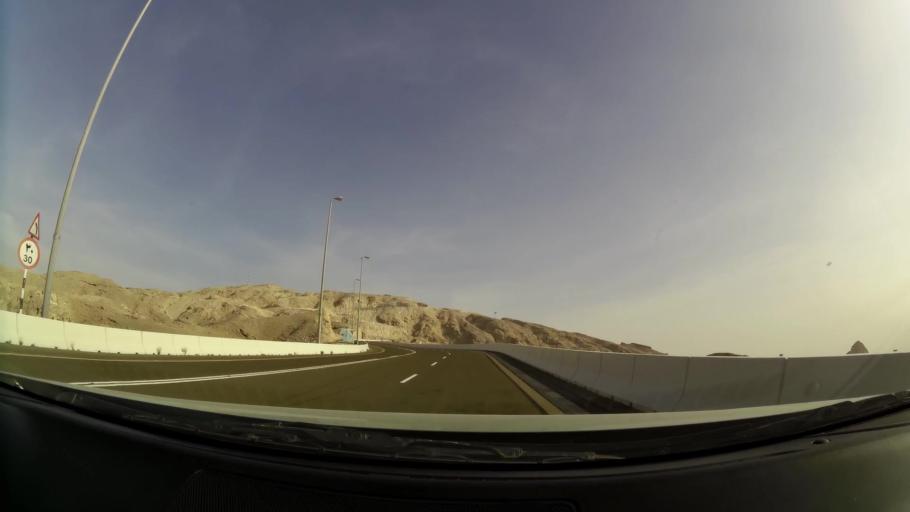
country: AE
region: Abu Dhabi
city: Al Ain
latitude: 24.0929
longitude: 55.7626
